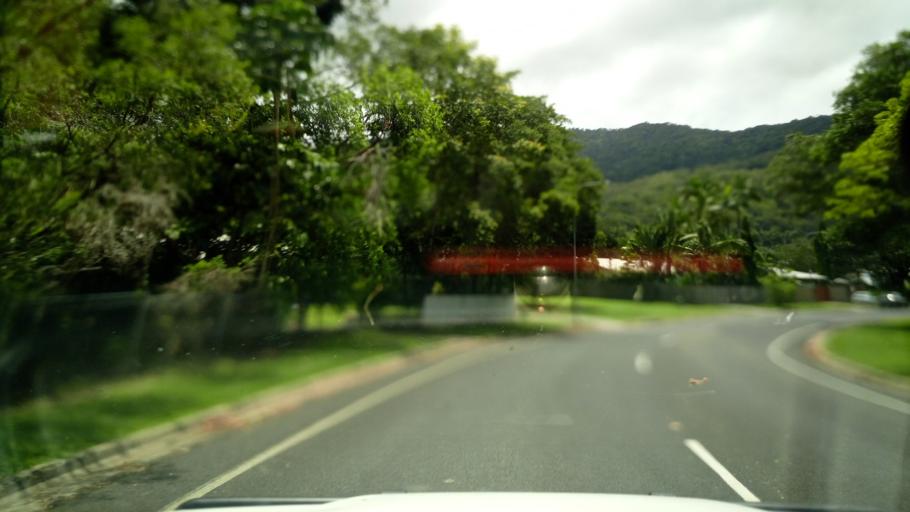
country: AU
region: Queensland
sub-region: Cairns
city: Yorkeys Knob
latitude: -16.8332
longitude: 145.6907
